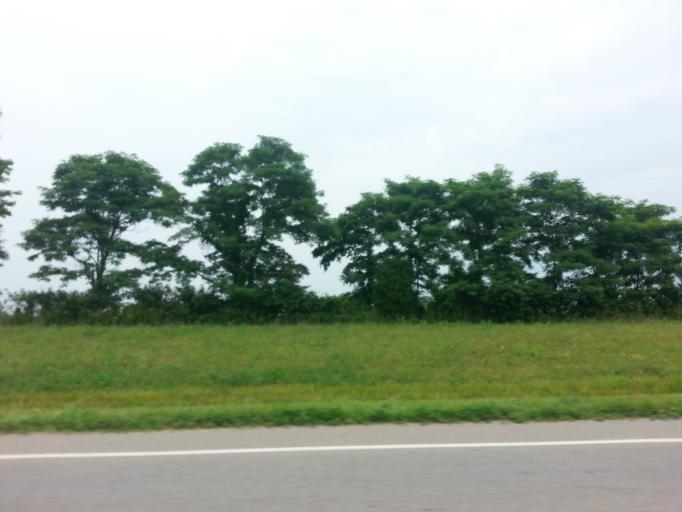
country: US
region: Ohio
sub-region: Brown County
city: Georgetown
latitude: 38.8765
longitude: -83.8871
